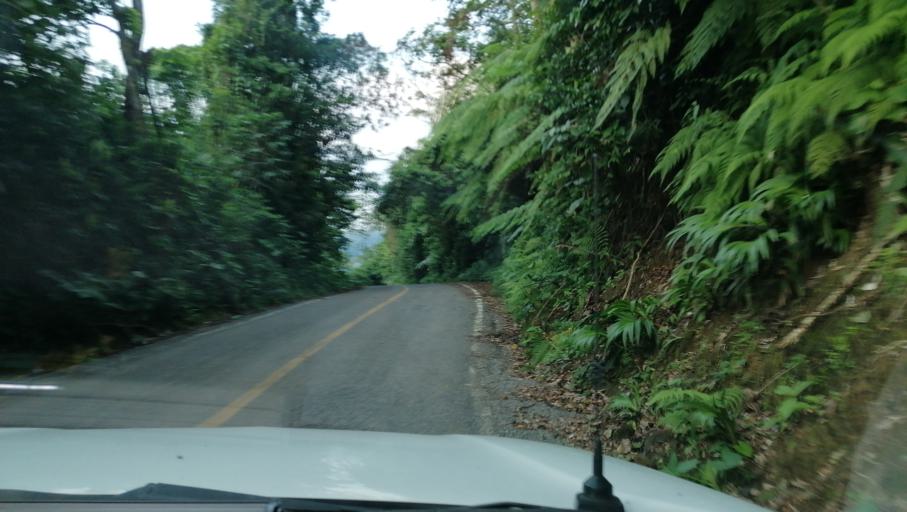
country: MX
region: Chiapas
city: Pichucalco
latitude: 17.5087
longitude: -93.2121
